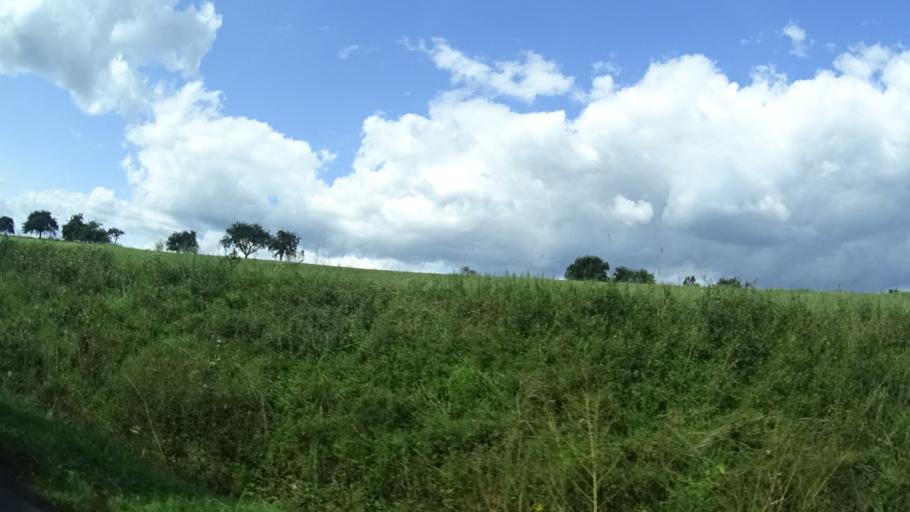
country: DE
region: Bavaria
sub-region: Regierungsbezirk Unterfranken
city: Breitbrunn
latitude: 50.0134
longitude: 10.7119
